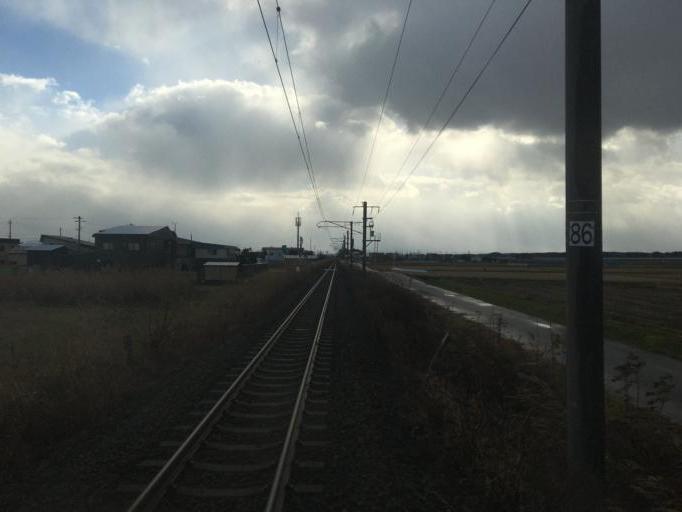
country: JP
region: Aomori
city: Aomori Shi
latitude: 40.8848
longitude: 140.6750
